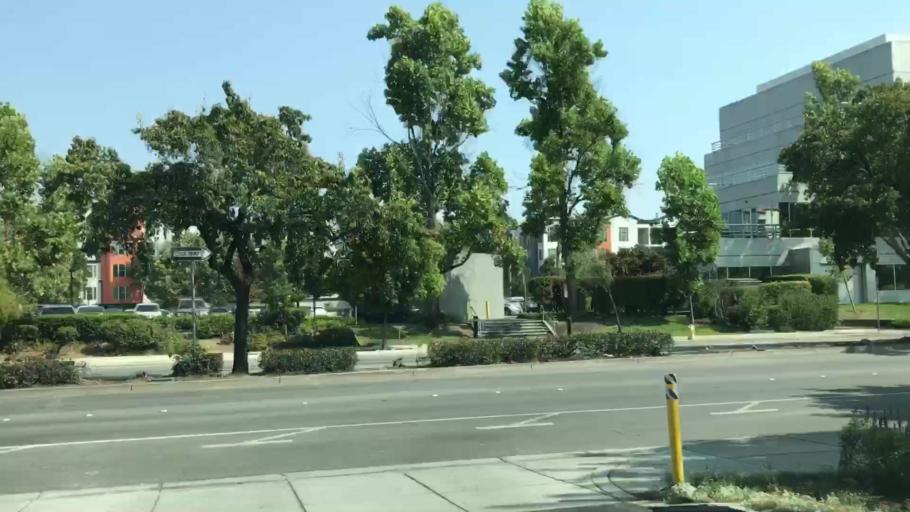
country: US
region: California
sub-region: Alameda County
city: Fremont
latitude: 37.5552
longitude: -121.9756
